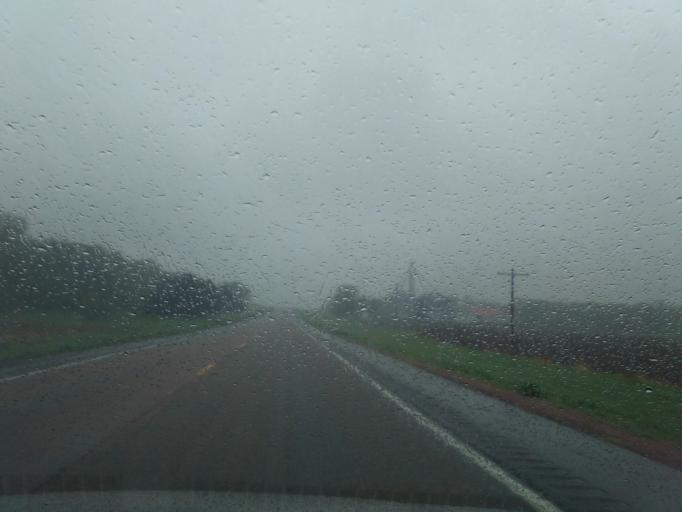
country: US
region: Nebraska
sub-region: Wayne County
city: Wayne
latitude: 42.2354
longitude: -97.0821
